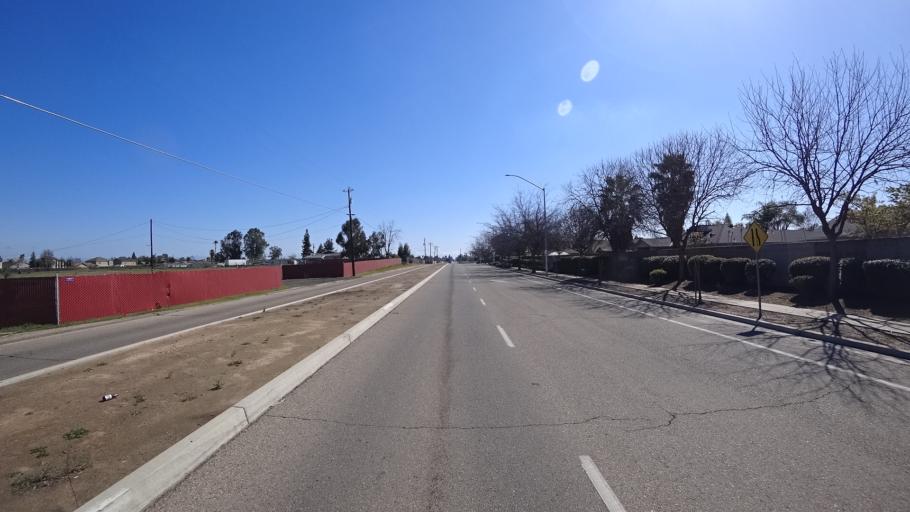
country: US
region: California
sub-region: Fresno County
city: West Park
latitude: 36.7645
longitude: -119.8928
